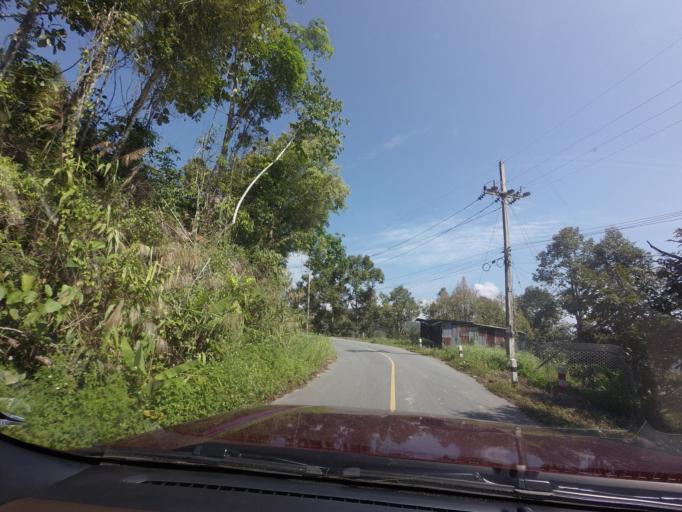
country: TH
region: Yala
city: Than To
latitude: 6.0088
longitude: 101.2269
